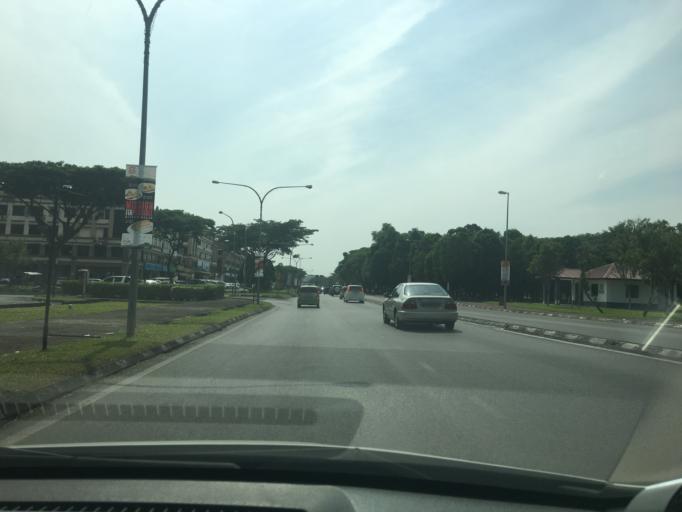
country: MY
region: Sarawak
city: Kuching
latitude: 1.5125
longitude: 110.3078
